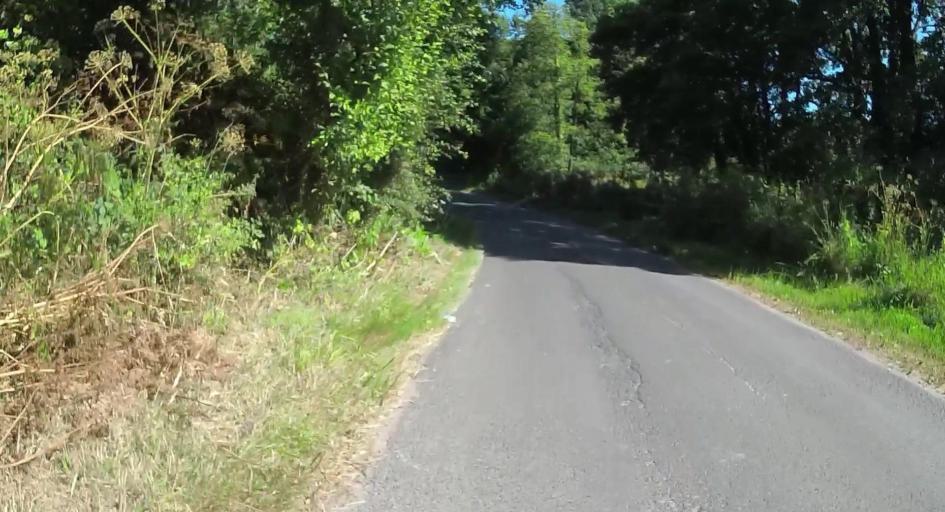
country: GB
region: England
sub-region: Dorset
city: Bovington Camp
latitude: 50.7273
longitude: -2.2014
